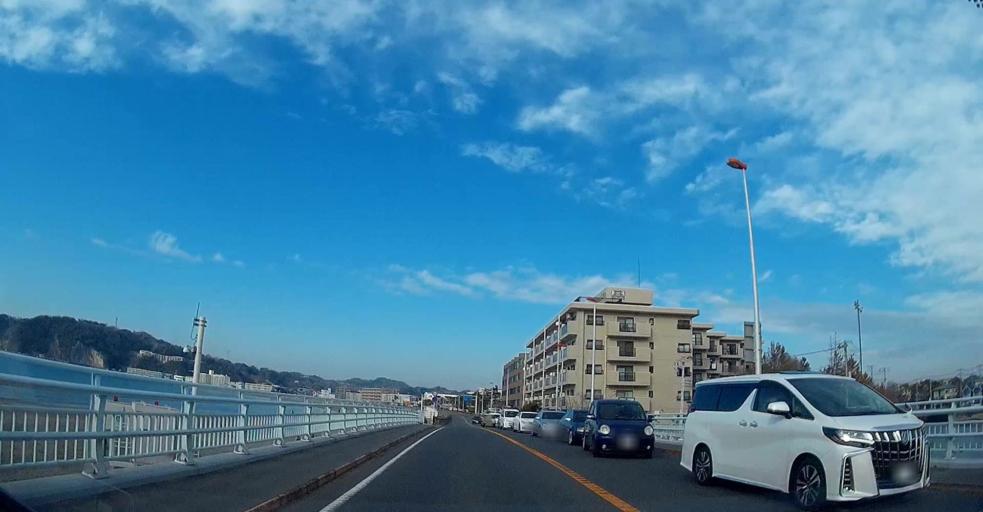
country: JP
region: Kanagawa
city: Zushi
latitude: 35.2862
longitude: 139.5727
